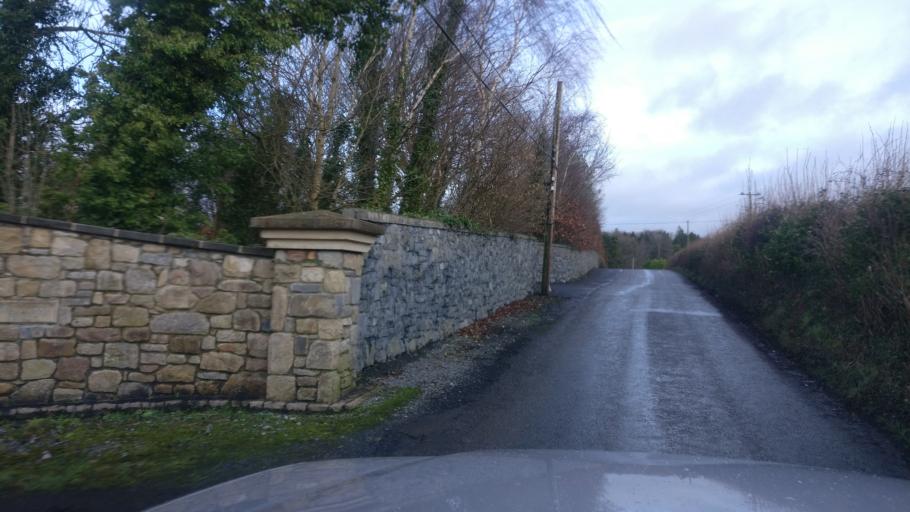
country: IE
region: Connaught
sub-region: County Galway
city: Athenry
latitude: 53.2484
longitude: -8.7199
